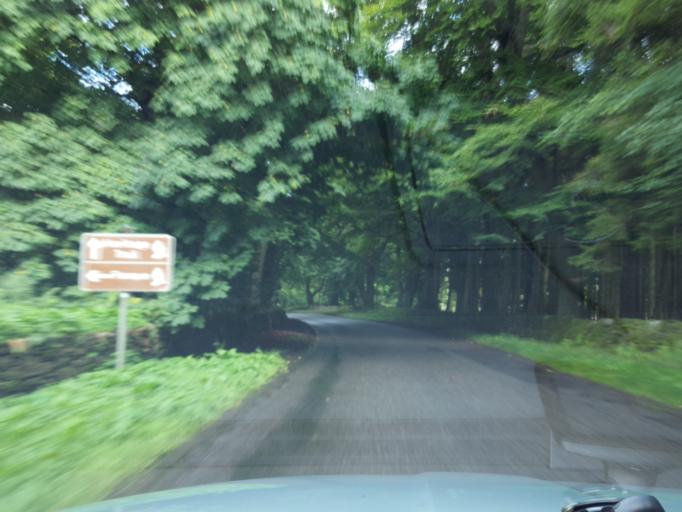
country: GB
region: Scotland
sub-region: Aberdeenshire
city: Laurencekirk
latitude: 56.8613
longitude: -2.5710
